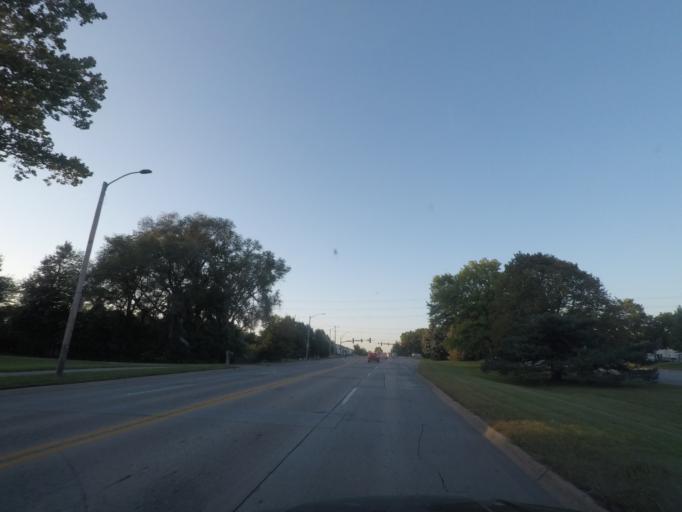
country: US
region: Iowa
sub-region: Story County
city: Ames
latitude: 42.0440
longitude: -93.6448
